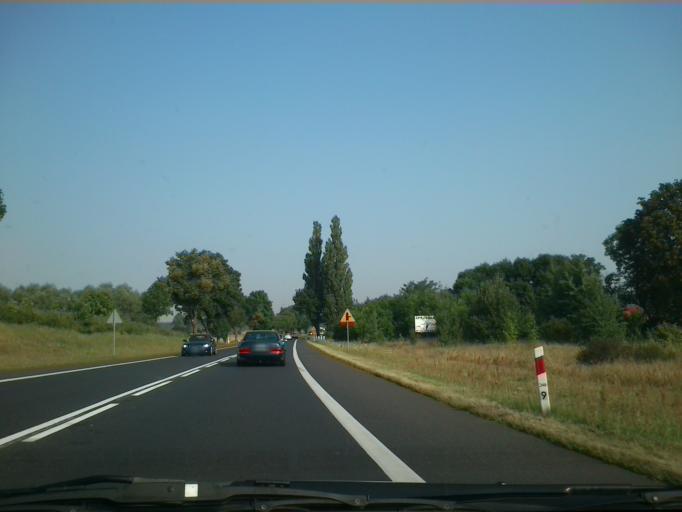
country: PL
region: Lower Silesian Voivodeship
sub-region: Powiat polkowicki
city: Radwanice
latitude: 51.5672
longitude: 16.0168
